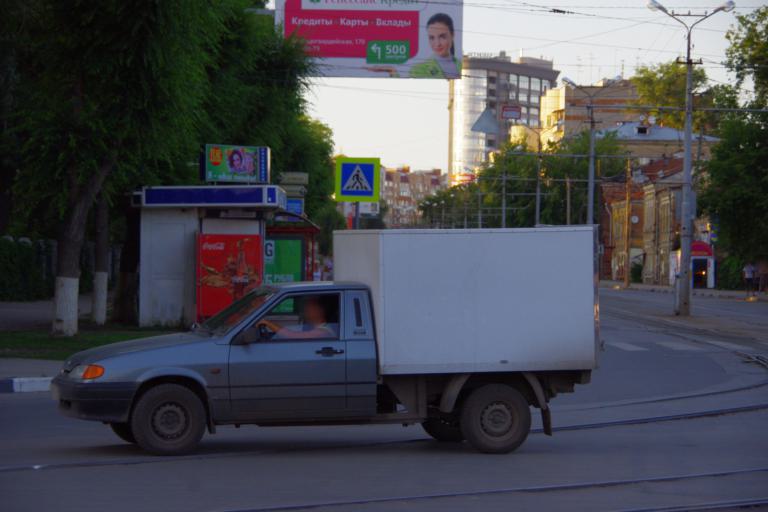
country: RU
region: Samara
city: Samara
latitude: 53.1929
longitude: 50.1027
